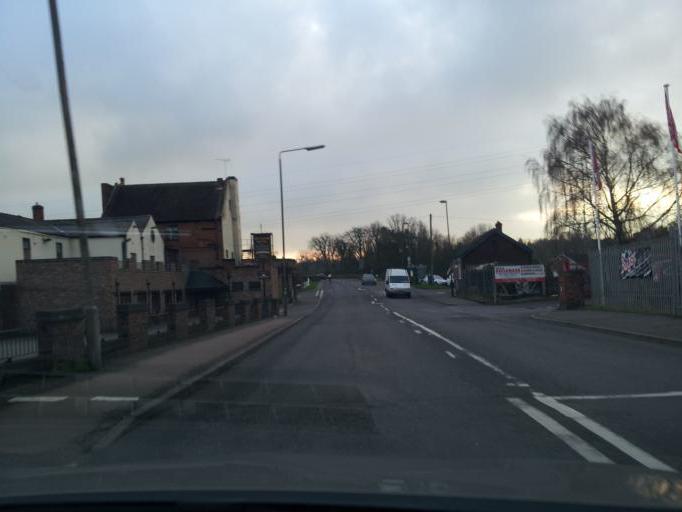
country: GB
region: England
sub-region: Staffordshire
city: Burton upon Trent
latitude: 52.8642
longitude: -1.6822
